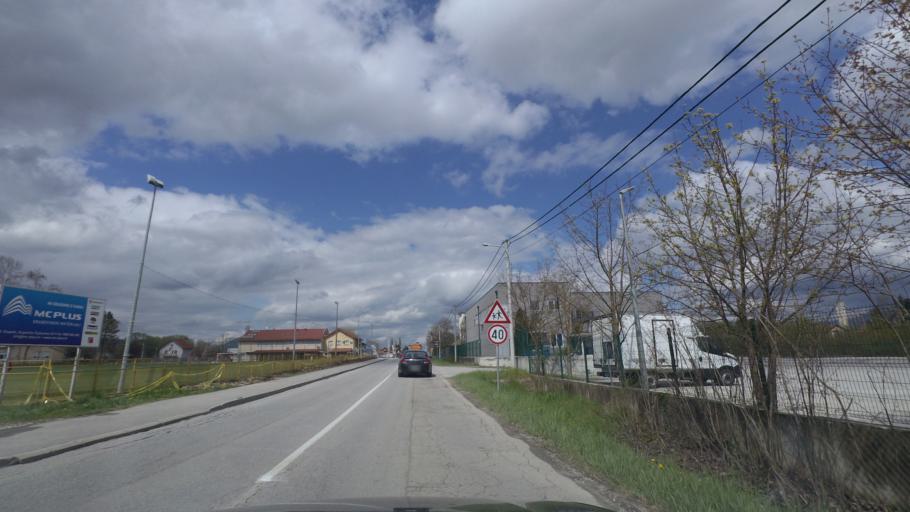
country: HR
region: Zagrebacka
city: Kerestinec
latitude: 45.7672
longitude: 15.8041
